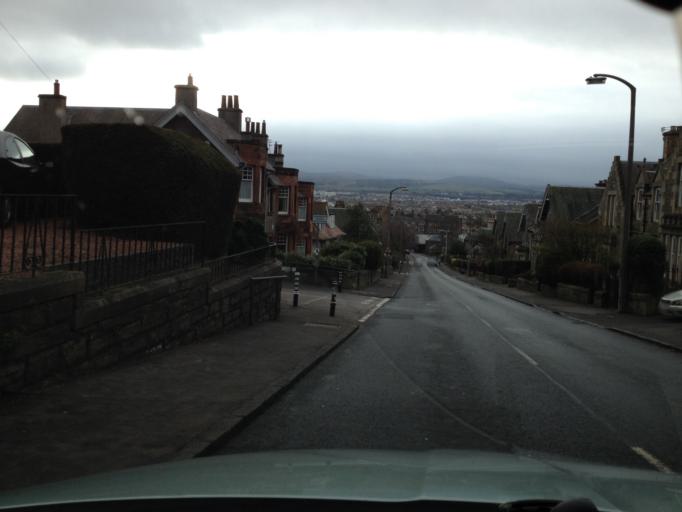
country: GB
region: Scotland
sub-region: Edinburgh
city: Colinton
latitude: 55.9453
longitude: -3.2805
